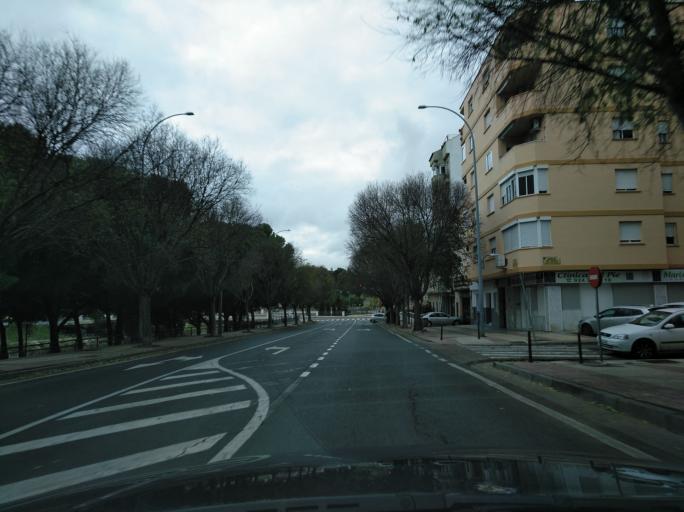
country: ES
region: Extremadura
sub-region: Provincia de Badajoz
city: Badajoz
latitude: 38.8780
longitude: -6.9616
